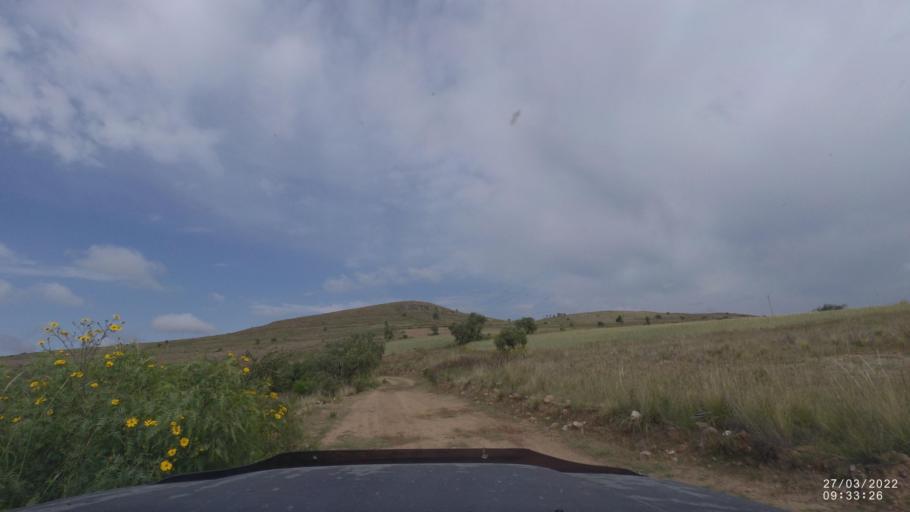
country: BO
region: Cochabamba
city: Cliza
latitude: -17.7399
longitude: -65.8889
